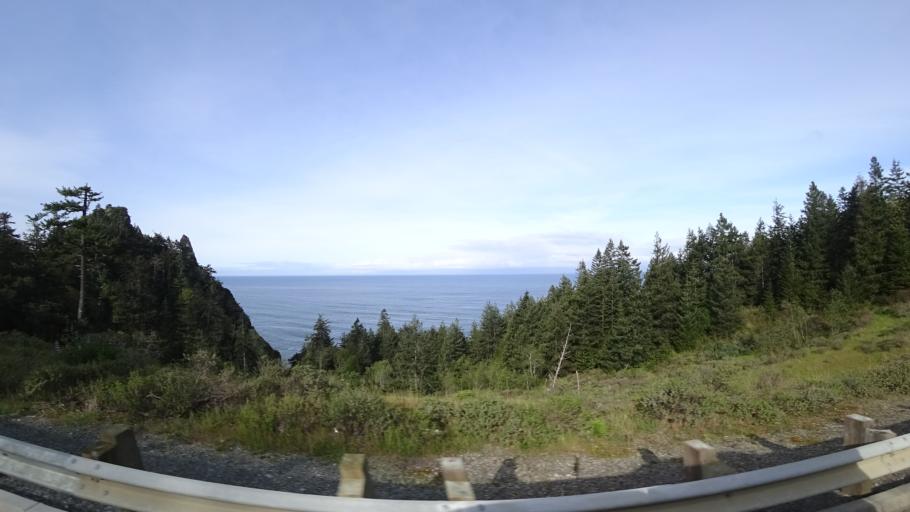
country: US
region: Oregon
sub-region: Curry County
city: Port Orford
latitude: 42.6375
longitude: -124.4027
